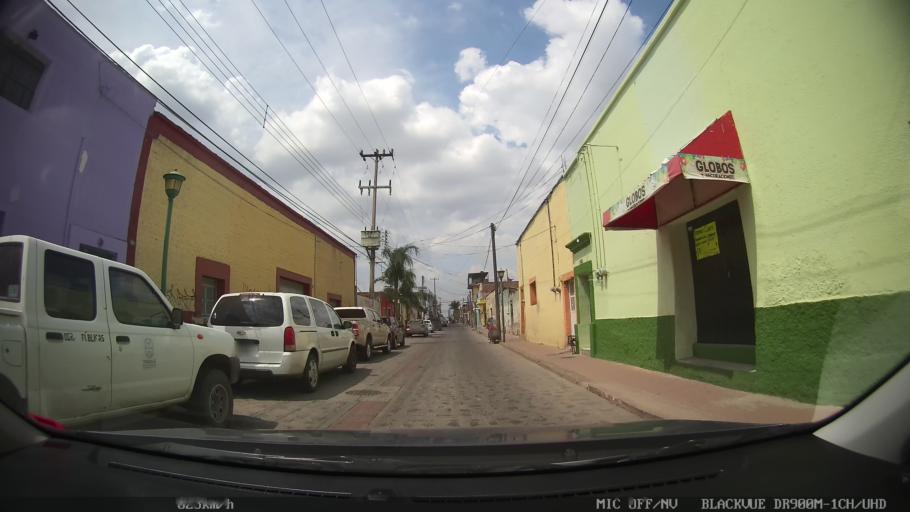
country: MX
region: Jalisco
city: Tonala
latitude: 20.6209
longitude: -103.2422
